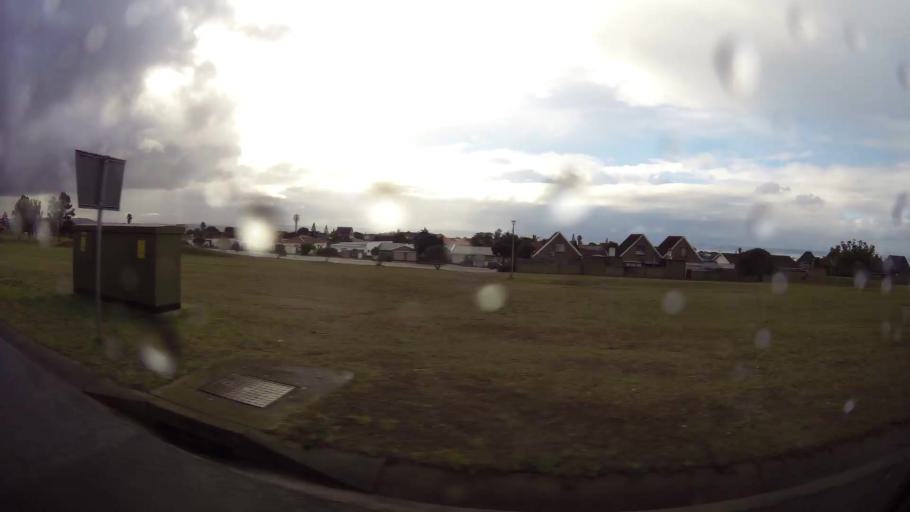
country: ZA
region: Western Cape
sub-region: Eden District Municipality
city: Mossel Bay
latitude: -34.1892
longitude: 22.1081
